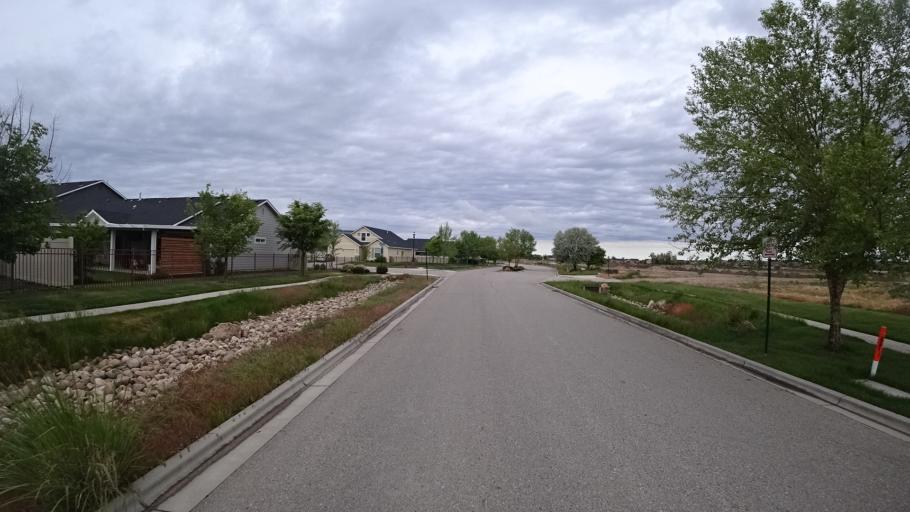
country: US
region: Idaho
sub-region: Ada County
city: Star
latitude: 43.7012
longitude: -116.4974
